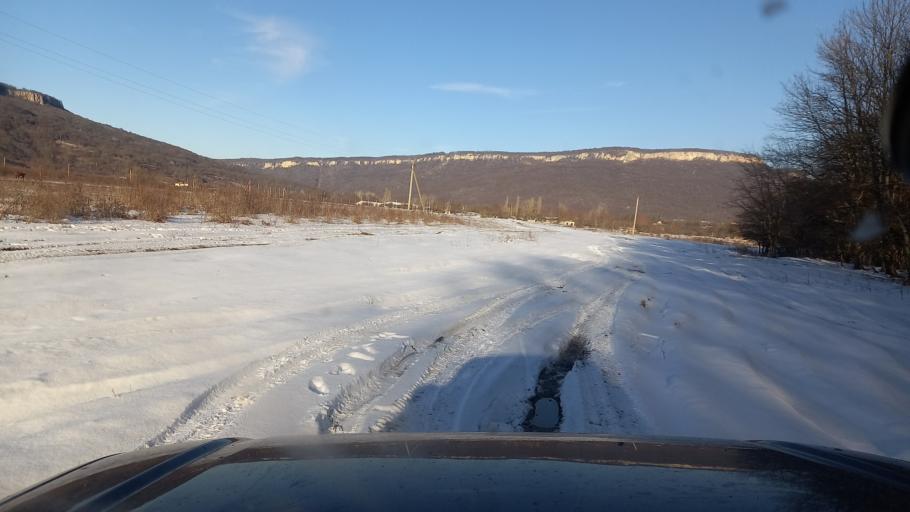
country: RU
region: Adygeya
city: Kamennomostskiy
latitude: 44.2178
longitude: 40.1779
